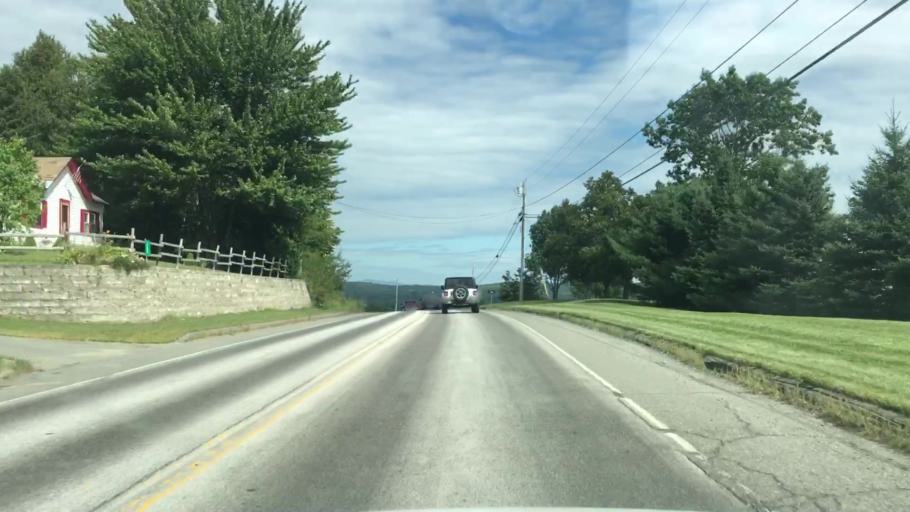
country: US
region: Maine
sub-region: Piscataquis County
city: Dover-Foxcroft
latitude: 45.1635
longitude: -69.2309
